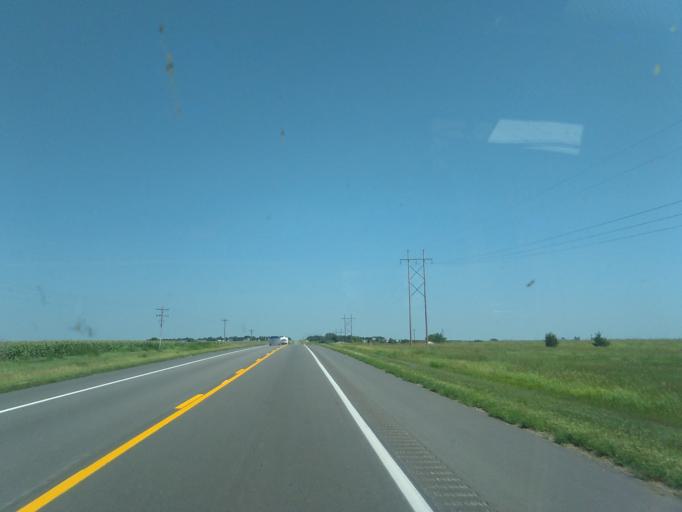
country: US
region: Nebraska
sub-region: Red Willow County
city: McCook
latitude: 40.2414
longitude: -100.6500
